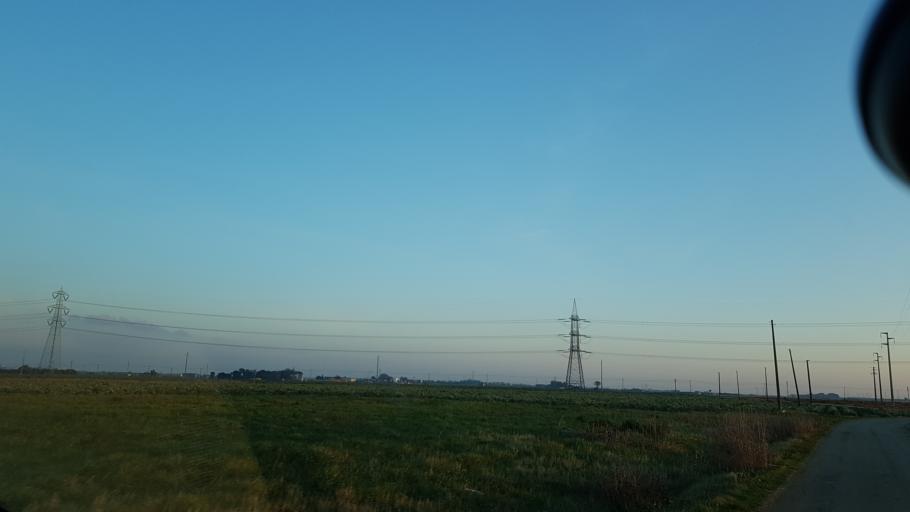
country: IT
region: Apulia
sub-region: Provincia di Brindisi
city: La Rosa
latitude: 40.5959
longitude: 17.9513
